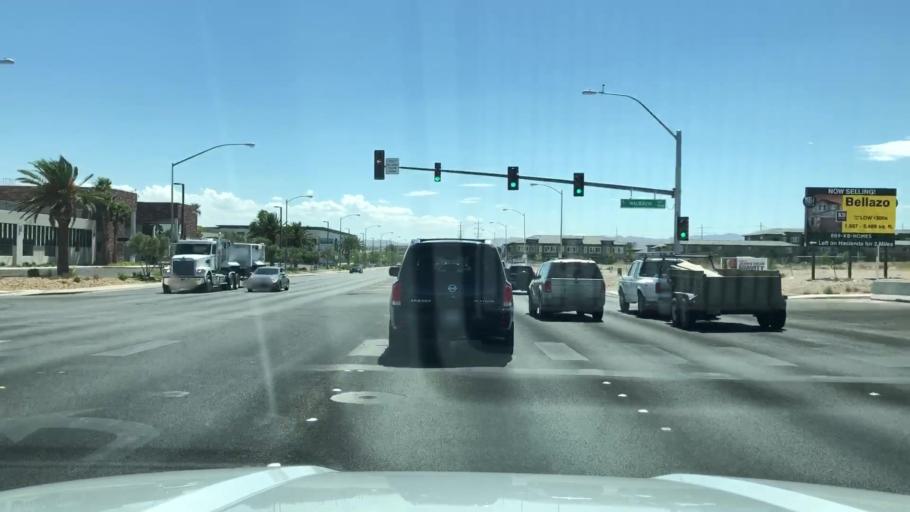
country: US
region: Nevada
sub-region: Clark County
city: Spring Valley
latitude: 36.0929
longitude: -115.2794
